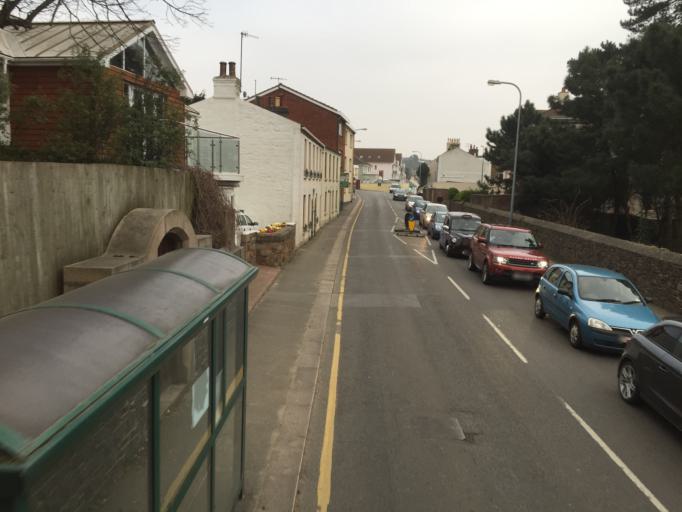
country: JE
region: St Helier
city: Saint Helier
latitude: 49.1987
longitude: -2.1400
